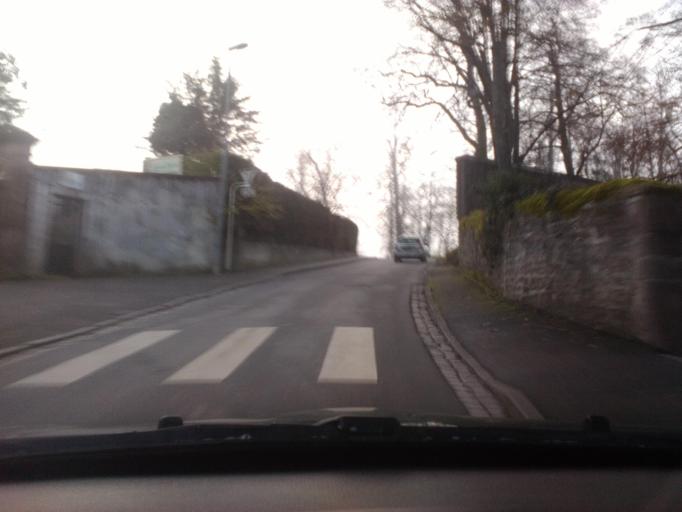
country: FR
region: Lorraine
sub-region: Departement des Vosges
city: Saint-Die-des-Vosges
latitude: 48.2898
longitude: 6.9520
